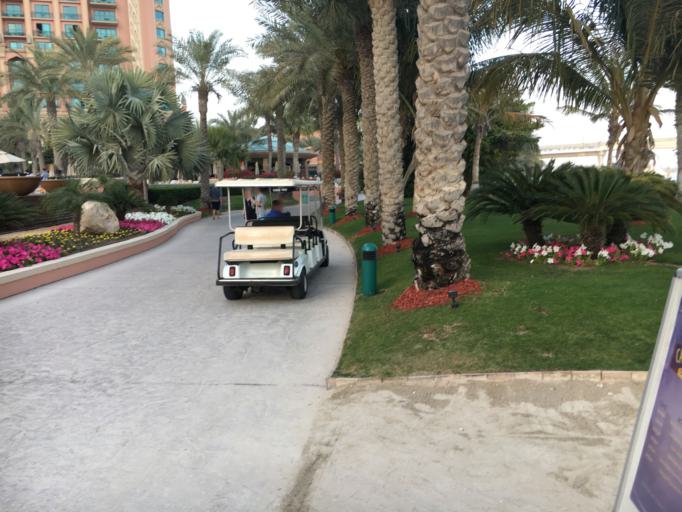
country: AE
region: Dubai
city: Dubai
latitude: 25.1298
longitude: 55.1179
